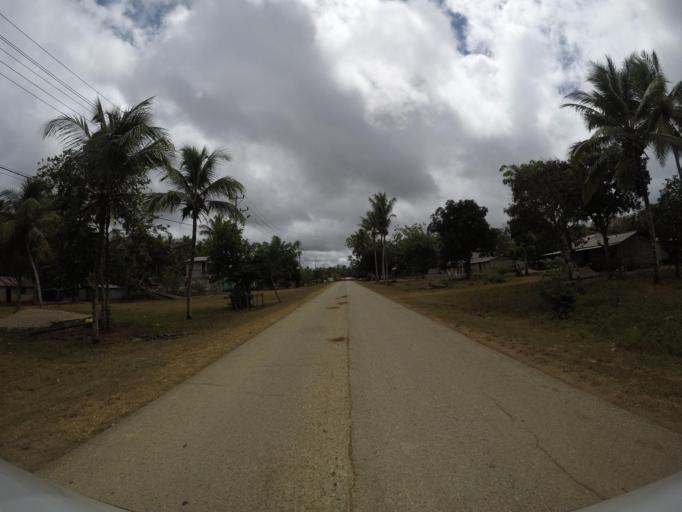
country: TL
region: Lautem
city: Lospalos
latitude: -8.4711
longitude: 126.9931
